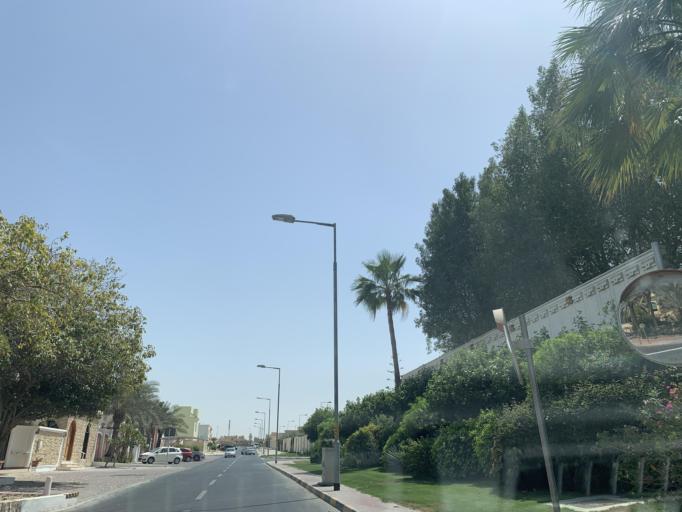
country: BH
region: Northern
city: Ar Rifa'
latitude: 26.1434
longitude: 50.5545
